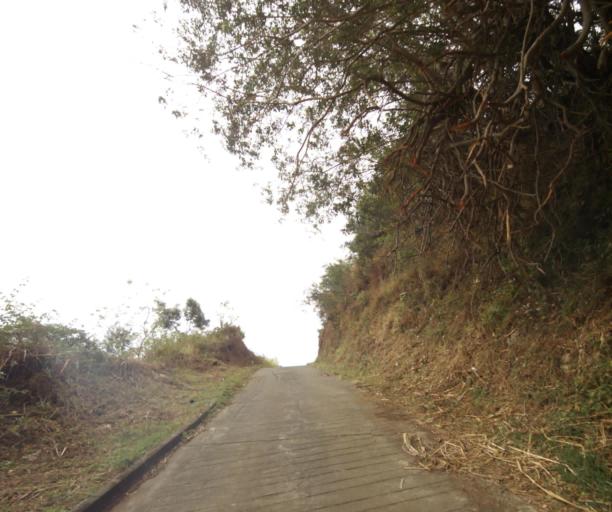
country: RE
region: Reunion
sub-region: Reunion
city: Saint-Paul
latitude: -21.0214
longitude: 55.3251
